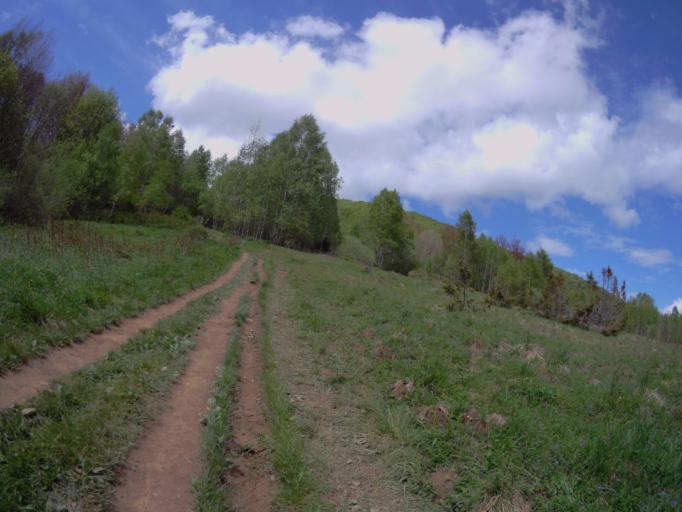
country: PL
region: Subcarpathian Voivodeship
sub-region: Powiat bieszczadzki
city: Lutowiska
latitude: 49.1427
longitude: 22.5667
